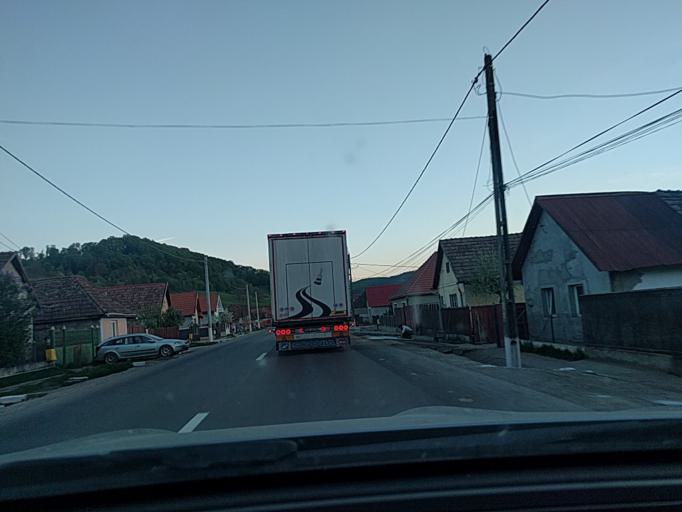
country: RO
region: Mures
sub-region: Comuna Nades
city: Nades
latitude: 46.3462
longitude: 24.7156
